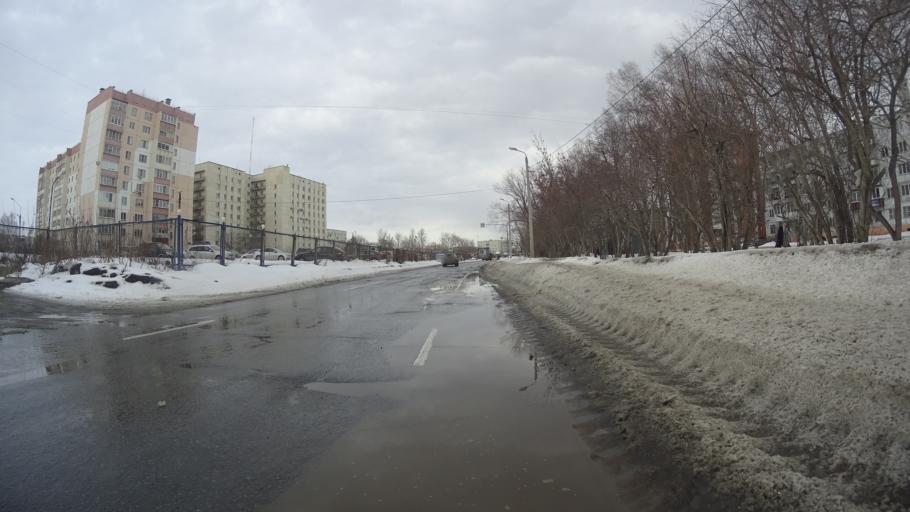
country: RU
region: Chelyabinsk
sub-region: Gorod Chelyabinsk
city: Chelyabinsk
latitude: 55.1992
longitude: 61.3223
